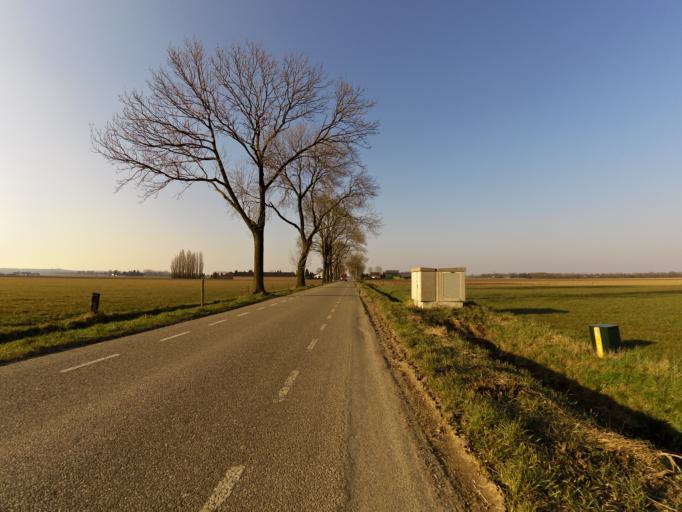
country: NL
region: Gelderland
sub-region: Gemeente Montferland
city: s-Heerenberg
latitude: 51.8674
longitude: 6.3055
